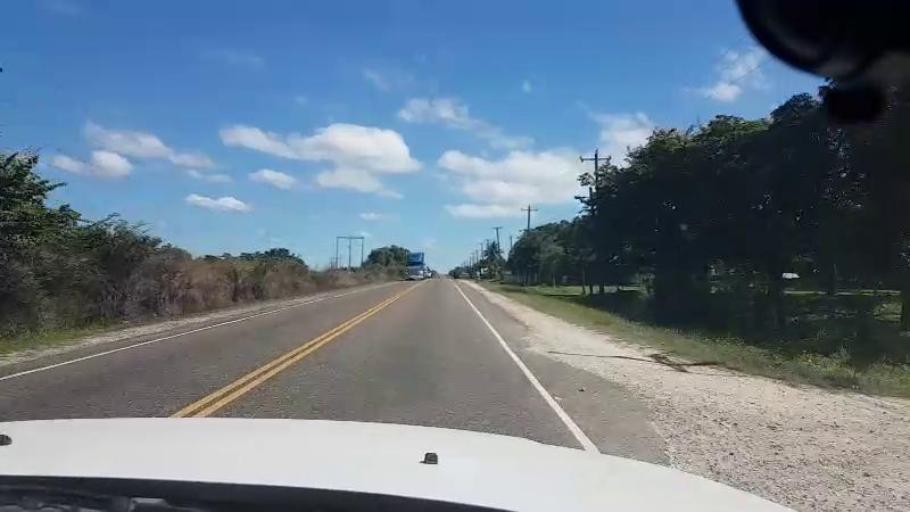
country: BZ
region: Cayo
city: Belmopan
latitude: 17.2769
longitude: -88.7171
